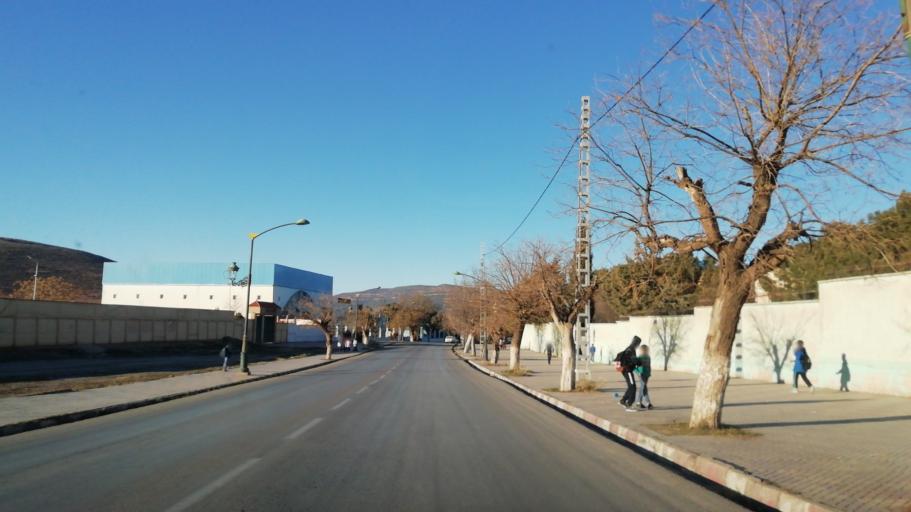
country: DZ
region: Tlemcen
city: Sebdou
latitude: 34.6344
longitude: -1.3332
